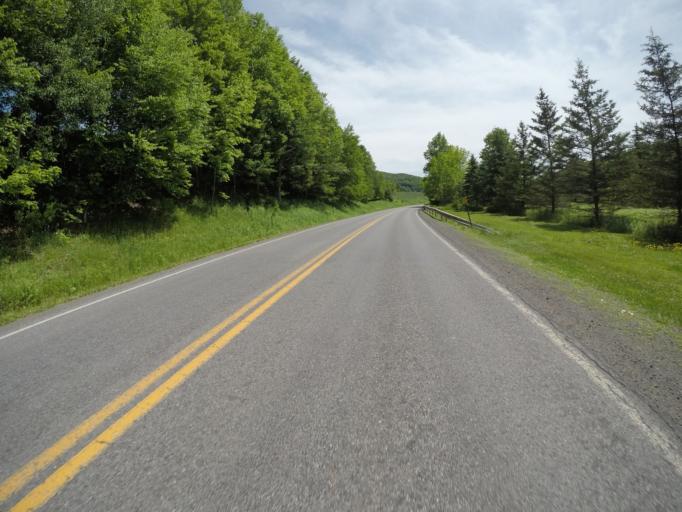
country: US
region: New York
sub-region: Delaware County
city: Delhi
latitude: 42.1738
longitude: -74.7893
